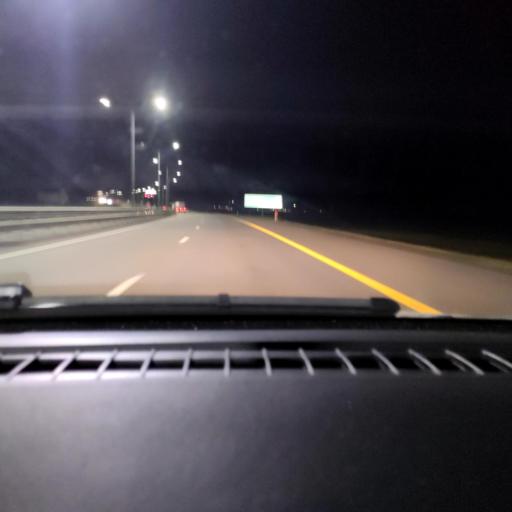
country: RU
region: Voronezj
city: Kashirskoye
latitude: 51.4860
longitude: 39.5353
